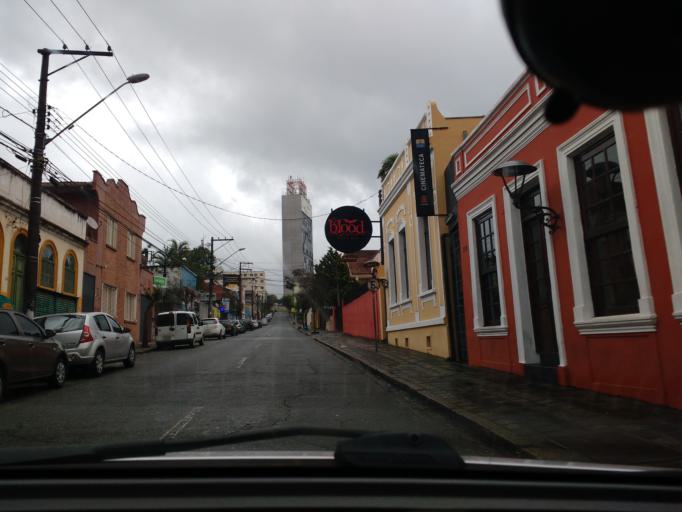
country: BR
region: Parana
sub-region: Curitiba
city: Curitiba
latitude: -25.4249
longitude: -49.2766
